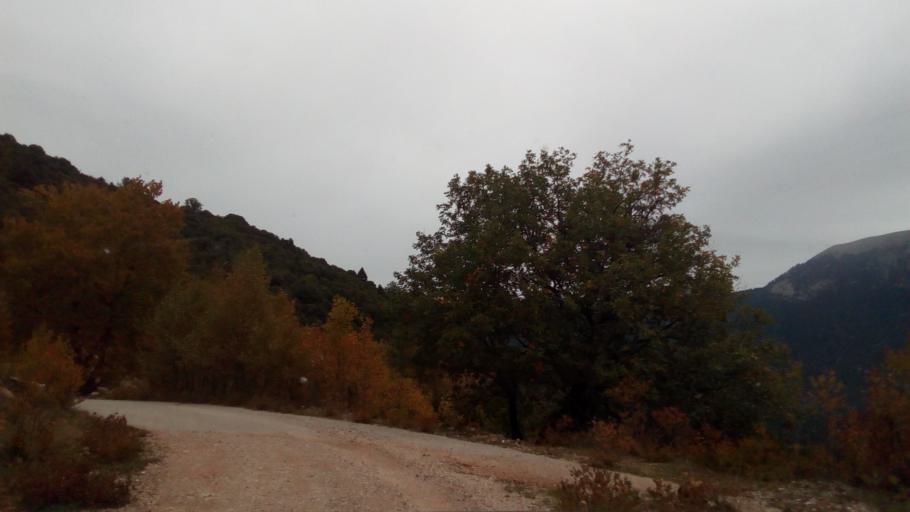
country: GR
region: West Greece
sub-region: Nomos Aitolias kai Akarnanias
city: Thermo
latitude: 38.6004
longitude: 21.8272
